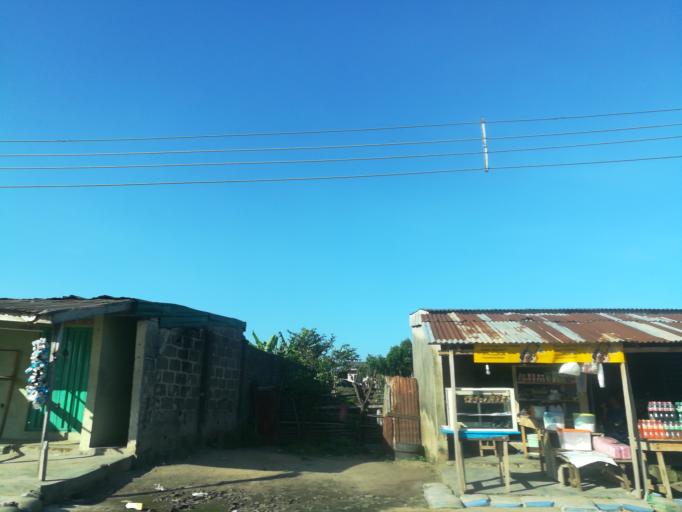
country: NG
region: Lagos
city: Ebute Ikorodu
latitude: 6.5400
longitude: 3.5496
